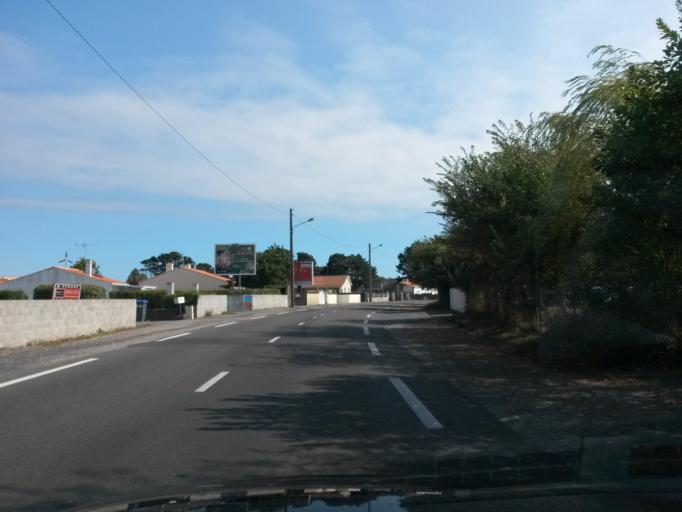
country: FR
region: Pays de la Loire
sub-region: Departement de la Vendee
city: Olonne-sur-Mer
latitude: 46.5523
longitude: -1.8069
